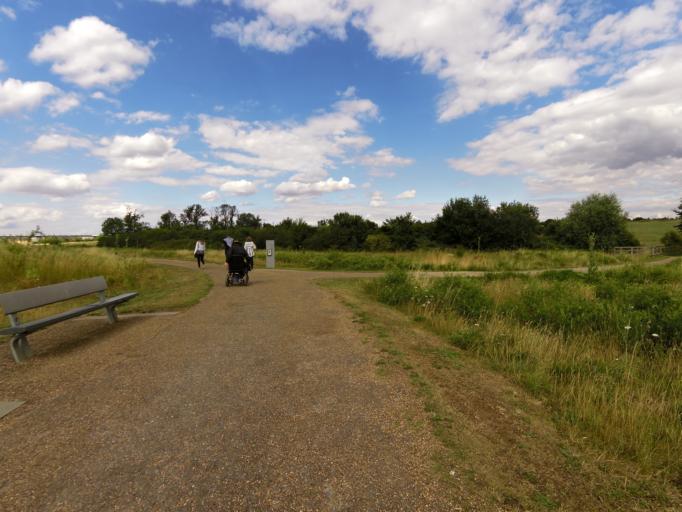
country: GB
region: England
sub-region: Essex
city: Waltham Abbey
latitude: 51.6721
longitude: -0.0053
